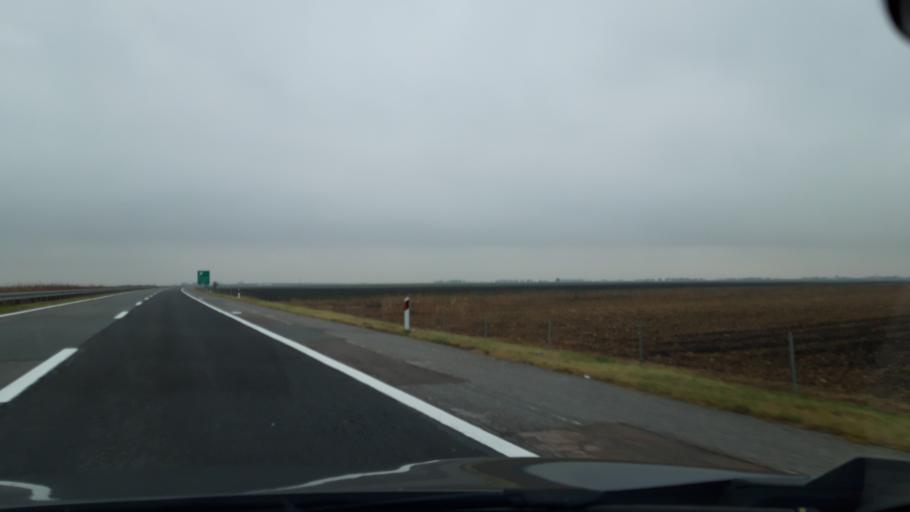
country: RS
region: Autonomna Pokrajina Vojvodina
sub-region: Severnobacki Okrug
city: Subotica
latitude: 45.9548
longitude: 19.7117
